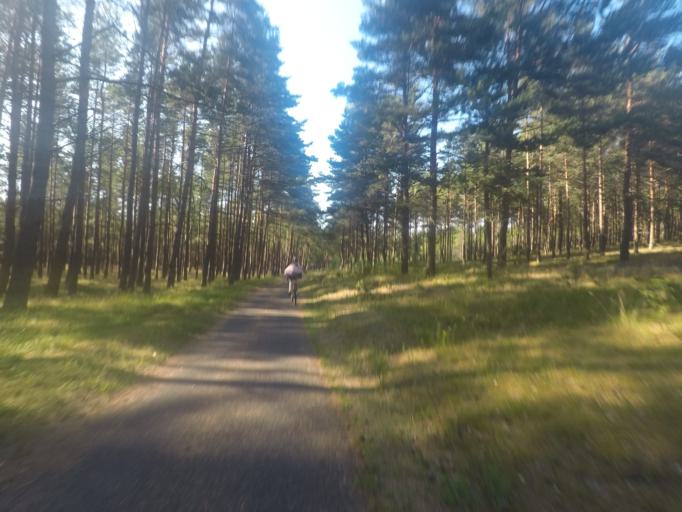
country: LT
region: Klaipedos apskritis
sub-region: Klaipeda
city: Klaipeda
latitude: 55.5794
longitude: 21.1140
